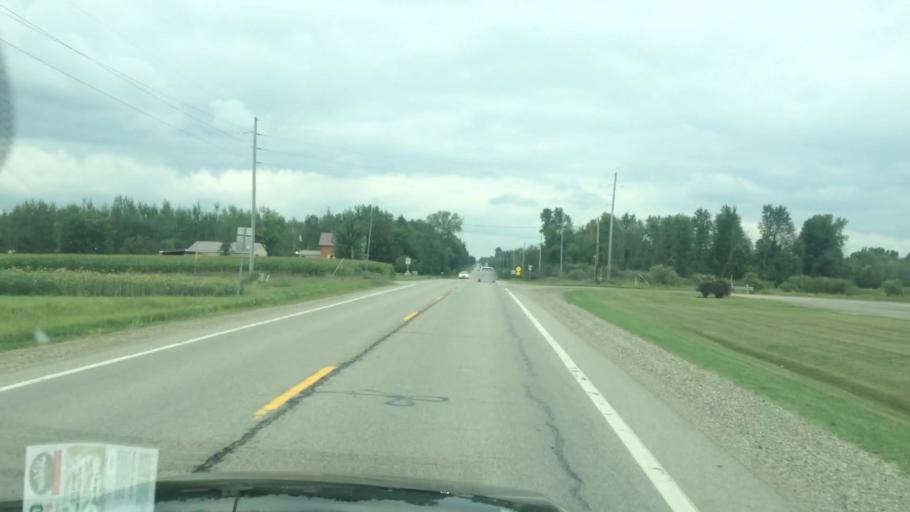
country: US
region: Michigan
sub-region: Sanilac County
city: Marlette
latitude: 43.4427
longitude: -83.0885
